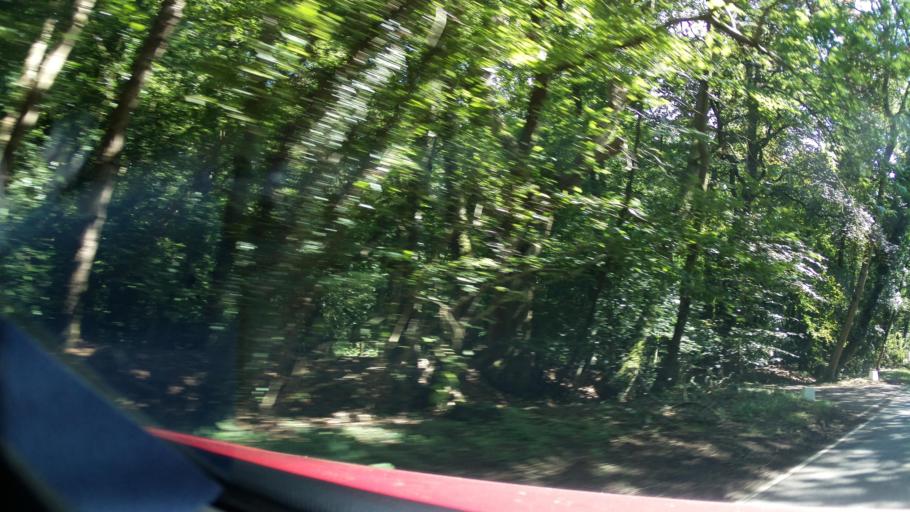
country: GB
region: England
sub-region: West Berkshire
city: Winterbourne
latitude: 51.4412
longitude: -1.3341
